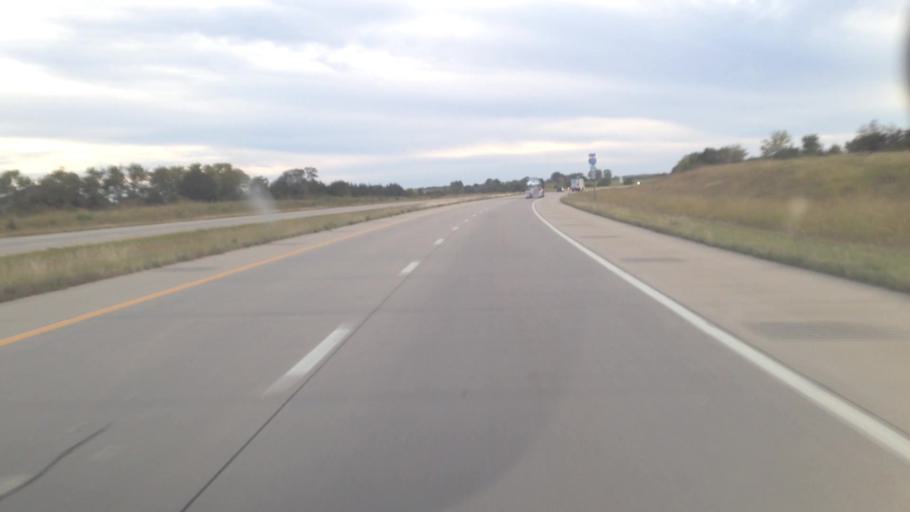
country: US
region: Kansas
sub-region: Franklin County
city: Ottawa
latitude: 38.5886
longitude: -95.2374
